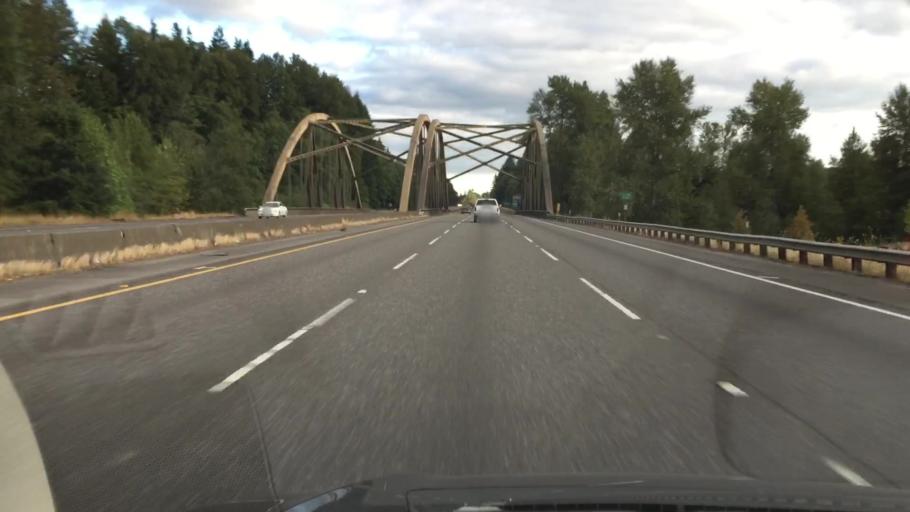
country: US
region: Washington
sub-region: Cowlitz County
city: Castle Rock
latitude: 46.3121
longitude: -122.9143
